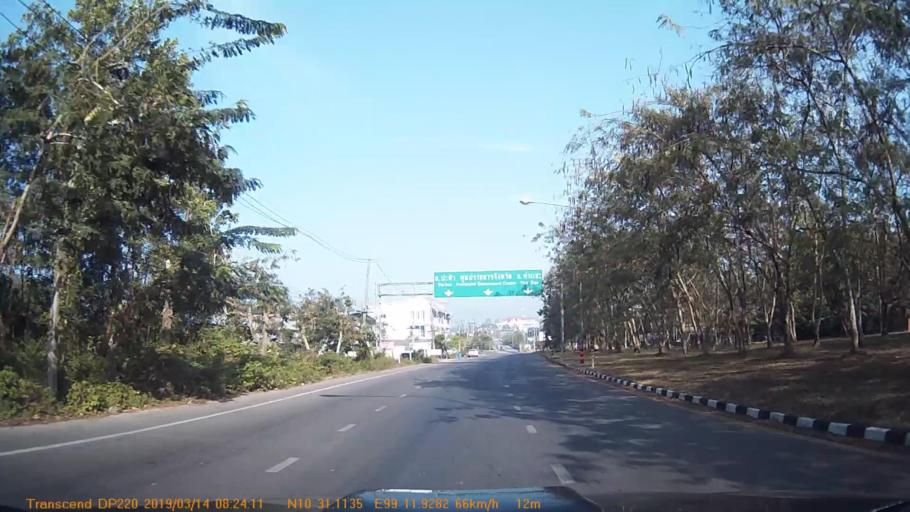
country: TH
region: Chumphon
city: Chumphon
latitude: 10.5186
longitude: 99.1987
